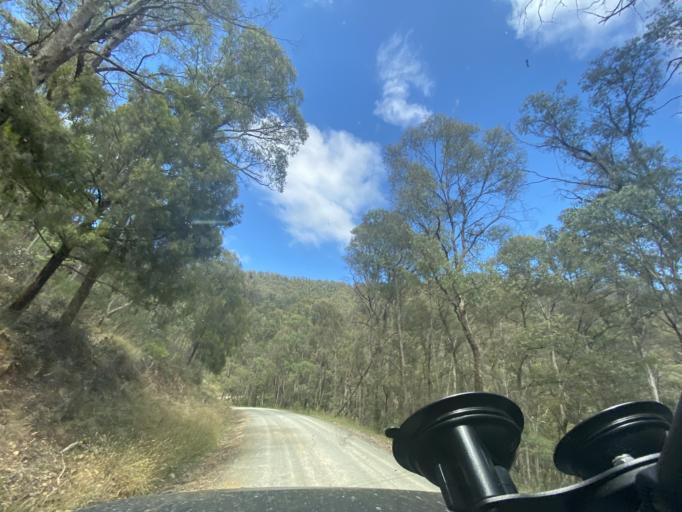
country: AU
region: Victoria
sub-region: Yarra Ranges
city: Millgrove
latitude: -37.5224
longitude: 146.0479
